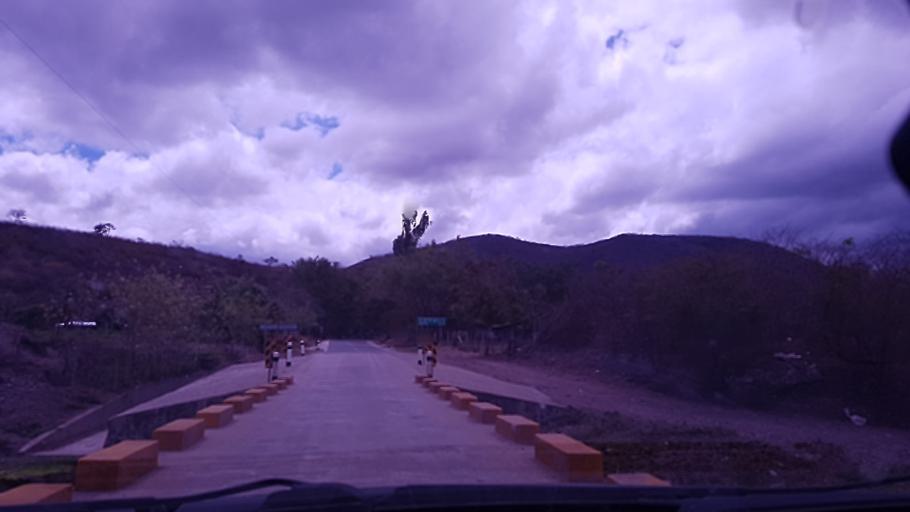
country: NI
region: Esteli
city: Condega
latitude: 13.3757
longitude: -86.3865
